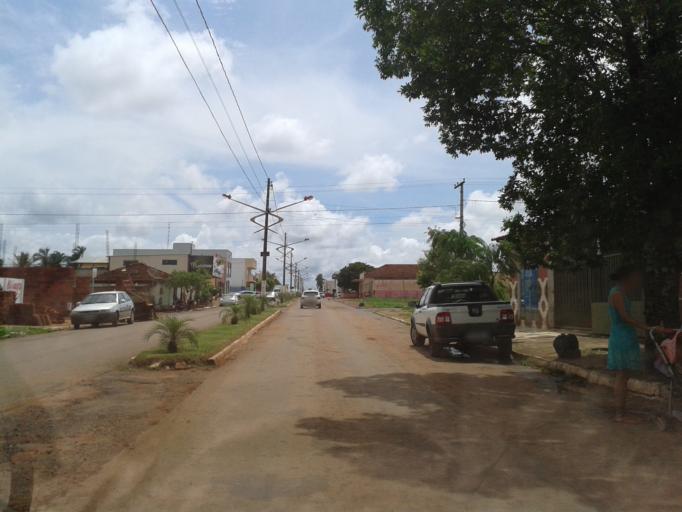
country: BR
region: Goias
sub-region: Buriti Alegre
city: Buriti Alegre
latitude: -18.1309
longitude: -49.0382
